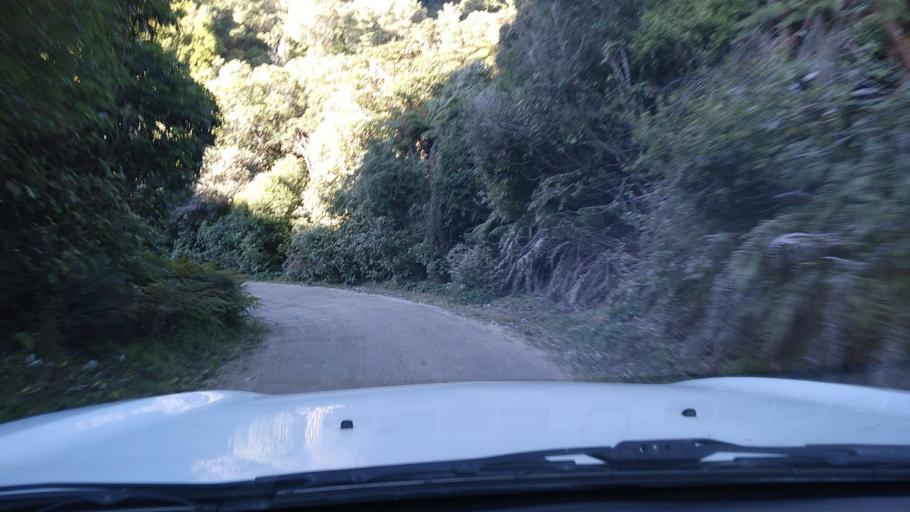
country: NZ
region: Waikato
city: Turangi
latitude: -38.6407
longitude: 175.6731
